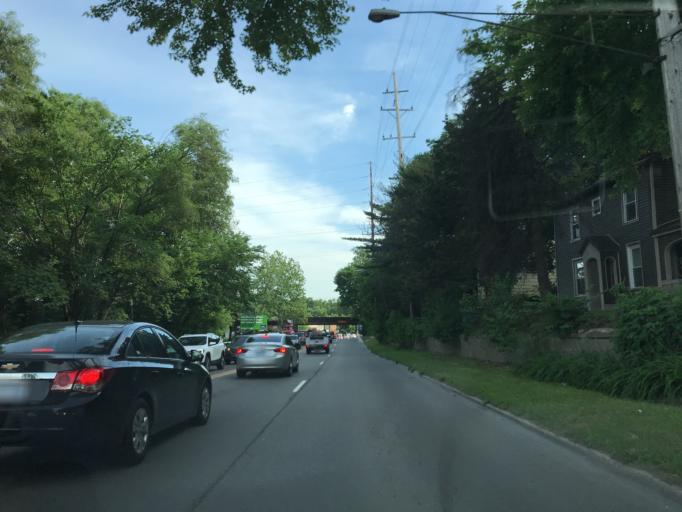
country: US
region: Michigan
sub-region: Washtenaw County
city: Ann Arbor
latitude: 42.2919
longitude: -83.7472
